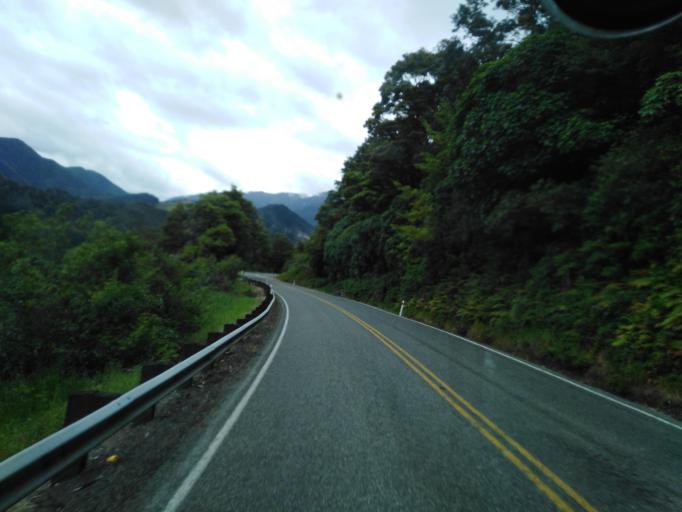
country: NZ
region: Tasman
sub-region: Tasman District
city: Wakefield
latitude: -41.7061
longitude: 172.5853
